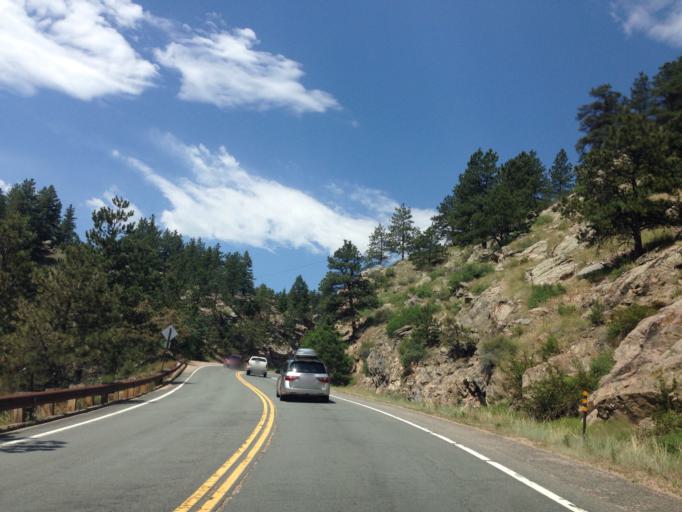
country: US
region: Colorado
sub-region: Larimer County
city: Estes Park
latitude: 40.4093
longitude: -105.3963
